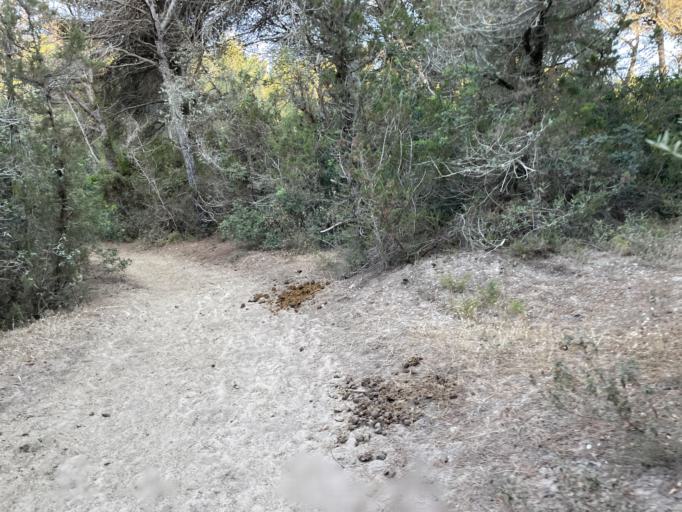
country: ES
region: Balearic Islands
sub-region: Illes Balears
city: Capdepera
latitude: 39.7151
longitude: 3.4536
